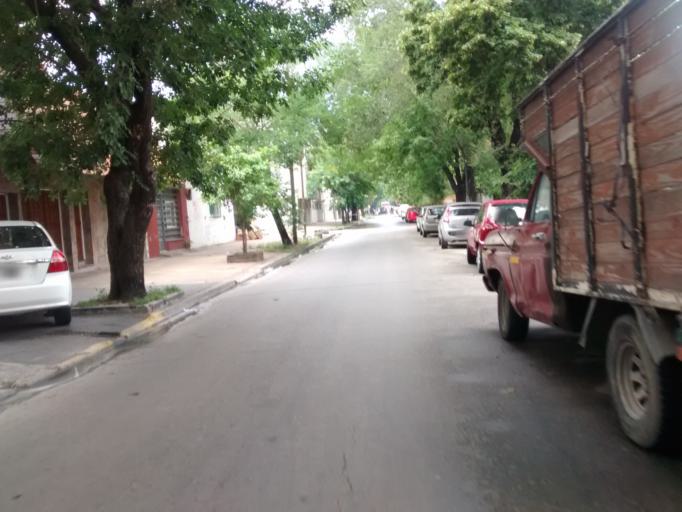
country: AR
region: Buenos Aires
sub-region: Partido de La Plata
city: La Plata
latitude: -34.9021
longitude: -57.9693
